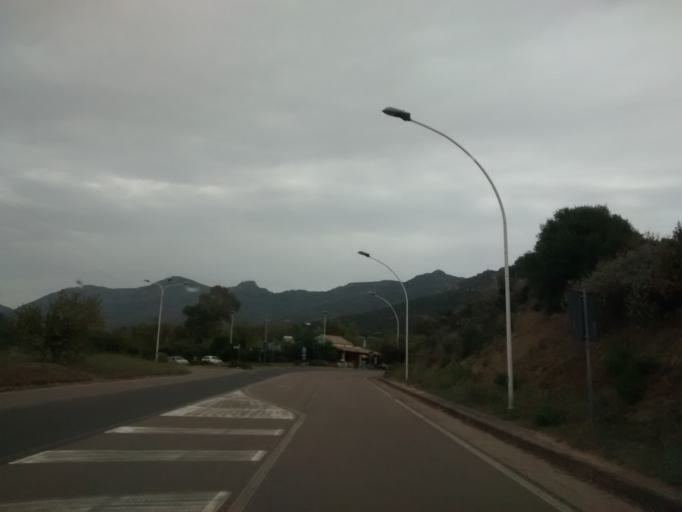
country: IT
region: Sardinia
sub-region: Provincia di Cagliari
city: Villasimius
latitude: 39.1429
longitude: 9.4336
